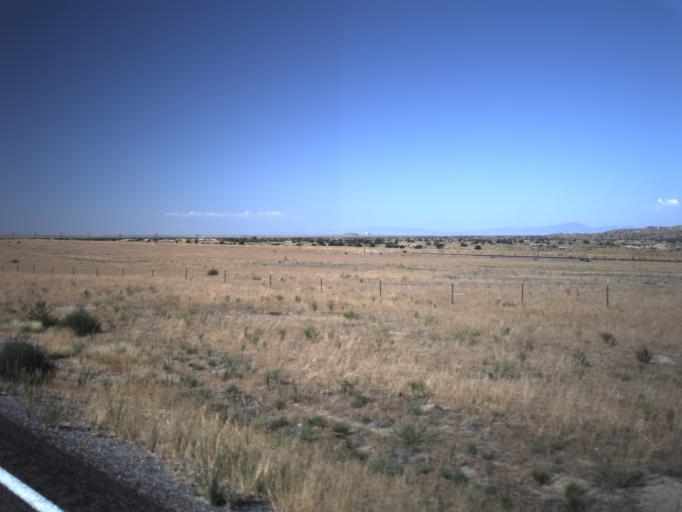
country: US
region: Utah
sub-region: Millard County
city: Delta
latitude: 39.6252
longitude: -112.3123
